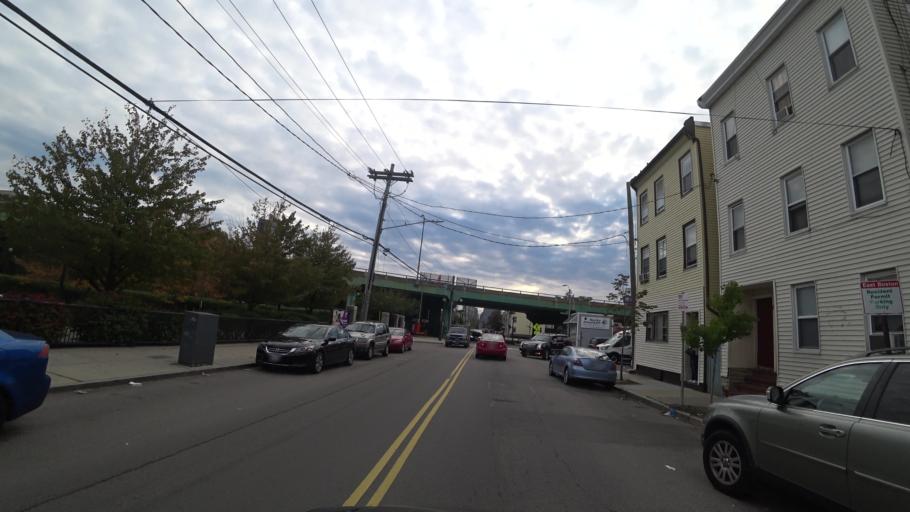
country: US
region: Massachusetts
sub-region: Suffolk County
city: Chelsea
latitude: 42.3732
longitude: -71.0339
